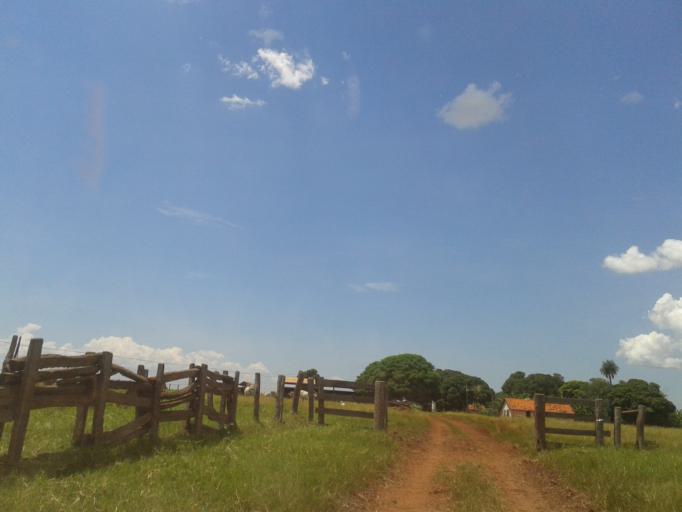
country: BR
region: Minas Gerais
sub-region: Santa Vitoria
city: Santa Vitoria
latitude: -19.1631
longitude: -50.4218
